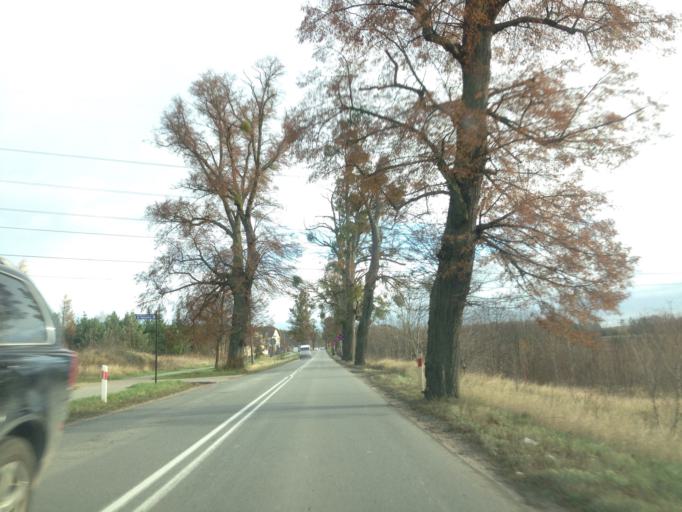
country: PL
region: Pomeranian Voivodeship
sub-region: Powiat gdanski
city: Lublewo Gdanskie
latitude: 54.2885
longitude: 18.5085
